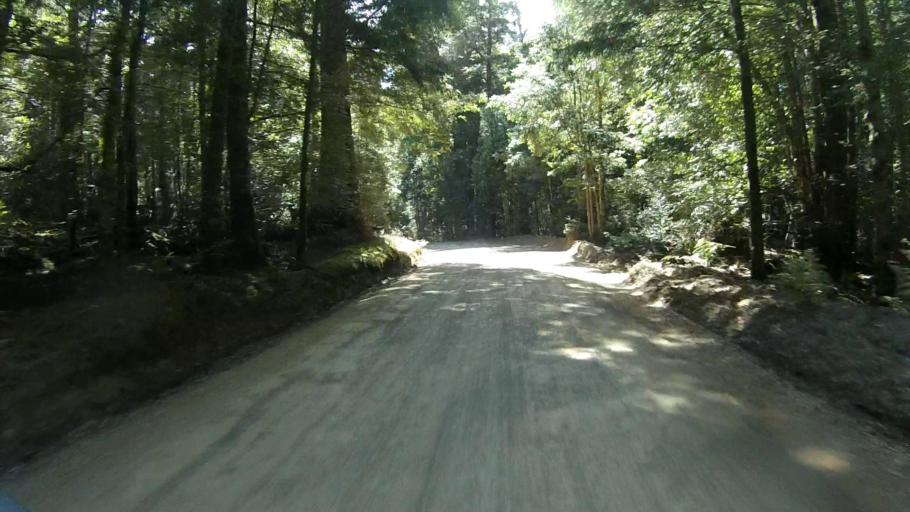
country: AU
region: Tasmania
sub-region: Derwent Valley
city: New Norfolk
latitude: -42.6808
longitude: 146.6687
